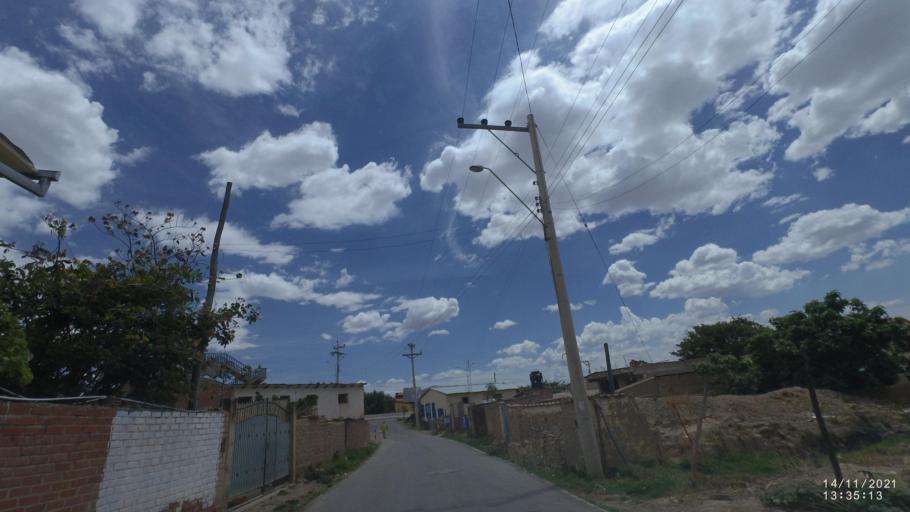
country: BO
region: Cochabamba
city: Colomi
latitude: -17.4068
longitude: -65.9869
